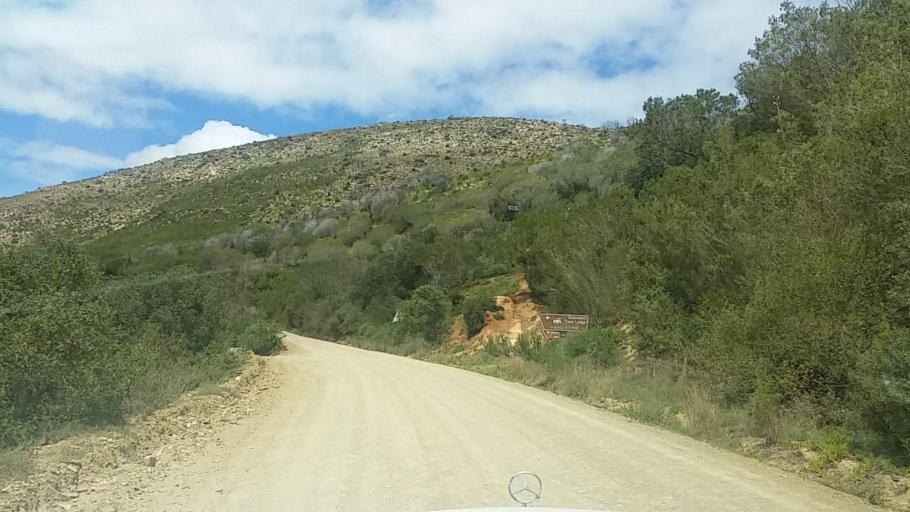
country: ZA
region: Western Cape
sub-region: Eden District Municipality
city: Knysna
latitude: -33.8172
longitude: 23.1740
